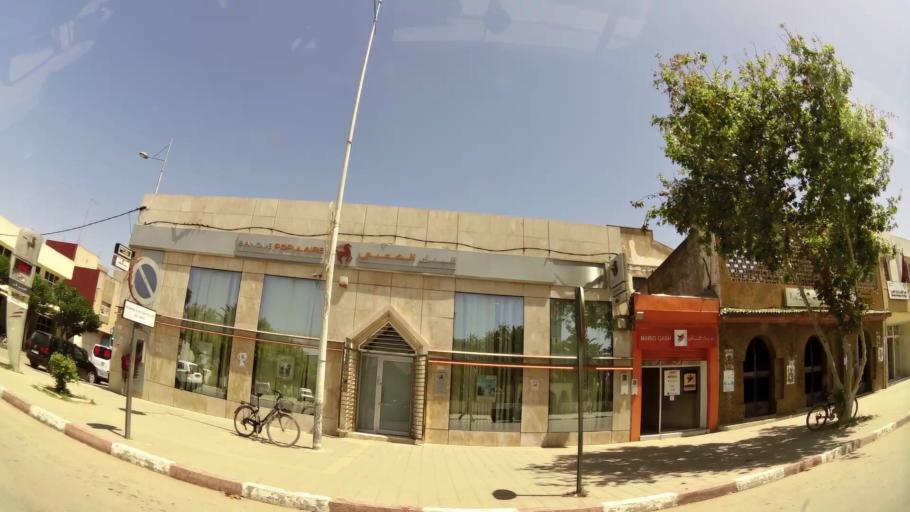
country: MA
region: Rabat-Sale-Zemmour-Zaer
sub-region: Khemisset
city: Khemisset
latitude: 33.8249
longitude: -6.0659
